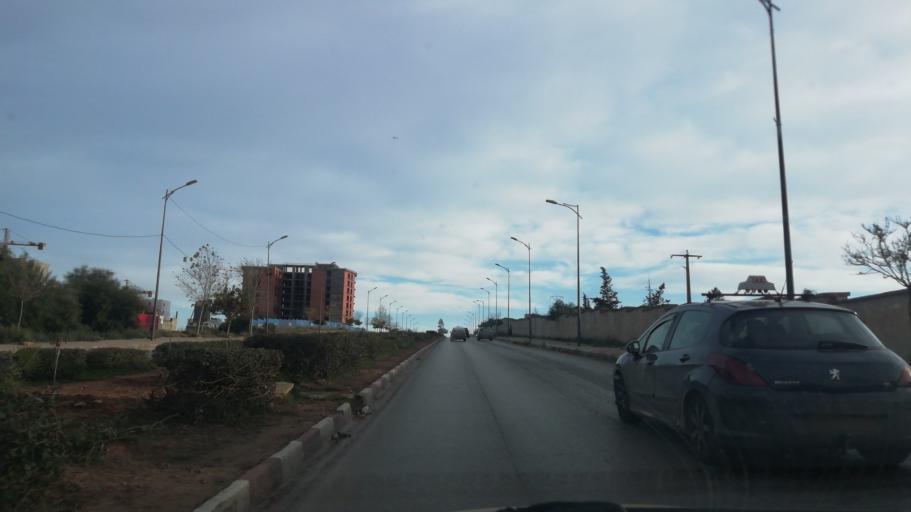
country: DZ
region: Oran
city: Bir el Djir
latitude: 35.7100
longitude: -0.5745
